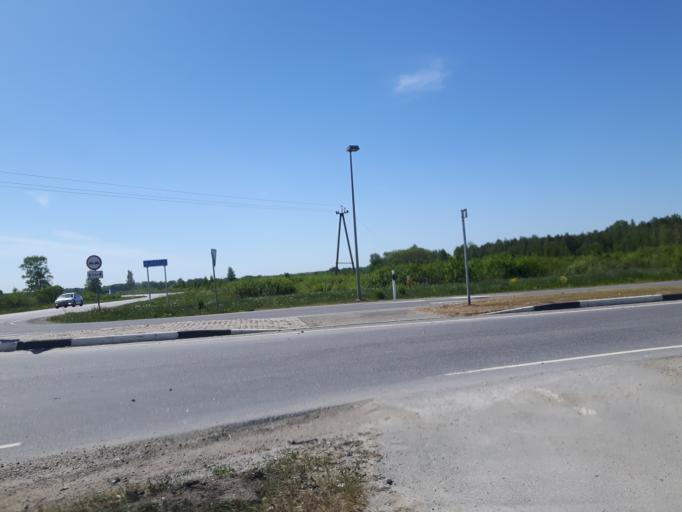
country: EE
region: Laeaene-Virumaa
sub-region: Viru-Nigula vald
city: Kunda
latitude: 59.4936
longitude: 26.5064
